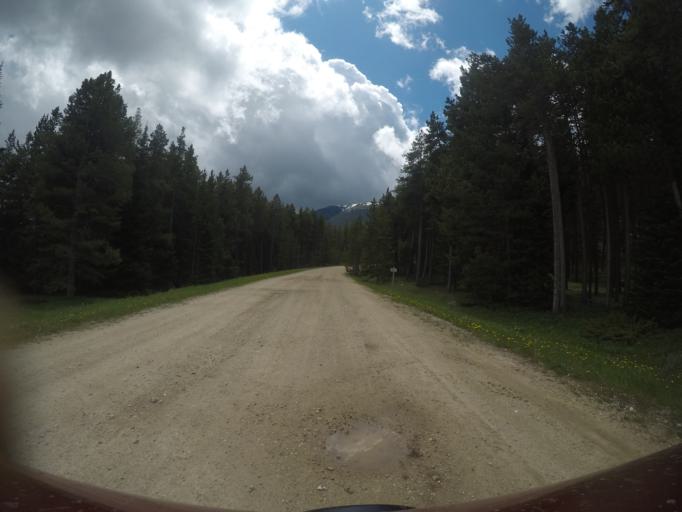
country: US
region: Wyoming
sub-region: Big Horn County
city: Lovell
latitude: 45.1775
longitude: -108.4496
